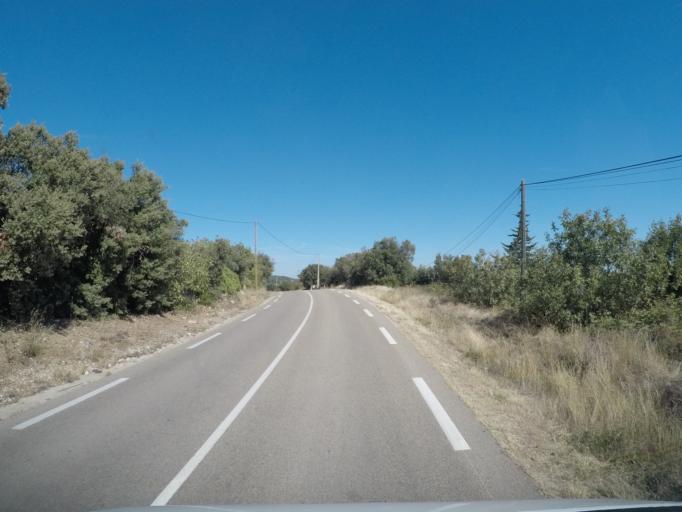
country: FR
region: Languedoc-Roussillon
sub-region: Departement de l'Herault
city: Saint-Martin-de-Londres
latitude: 43.7349
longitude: 3.6913
